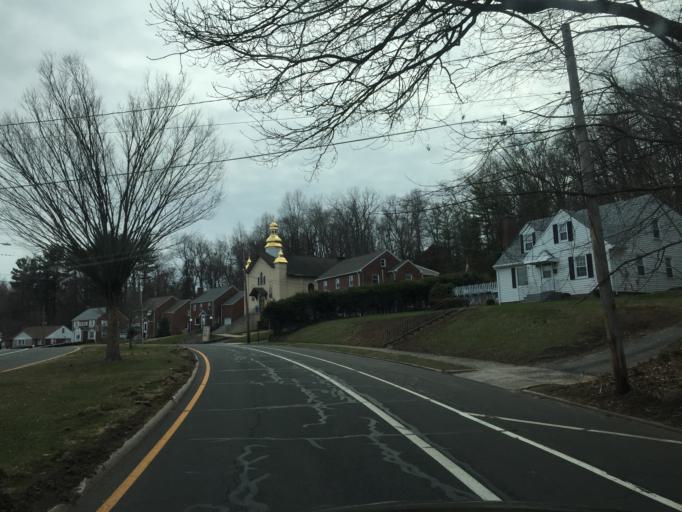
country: US
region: Connecticut
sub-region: Hartford County
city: New Britain
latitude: 41.6907
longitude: -72.7821
